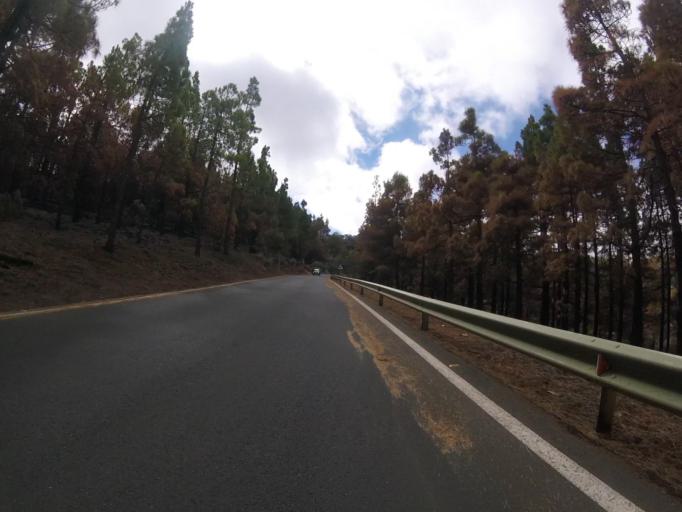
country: ES
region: Canary Islands
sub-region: Provincia de Las Palmas
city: San Bartolome
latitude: 27.9679
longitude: -15.5651
